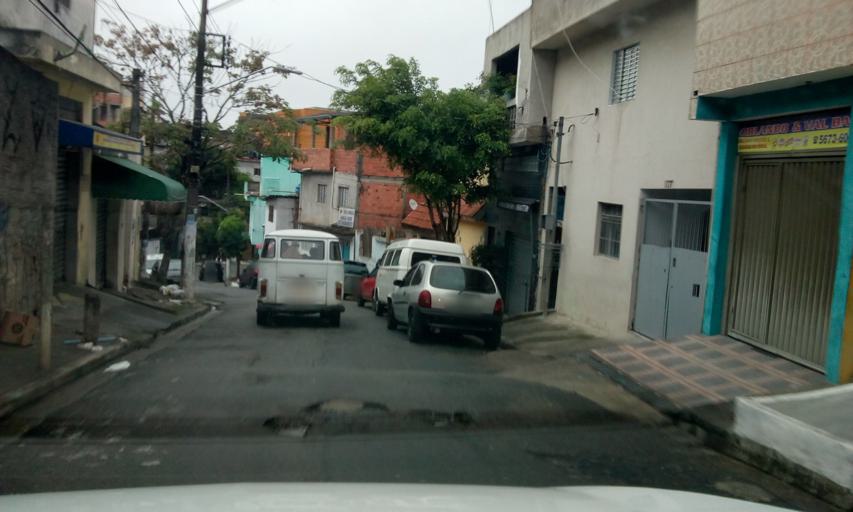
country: BR
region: Sao Paulo
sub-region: Diadema
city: Diadema
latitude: -23.6982
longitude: -46.6299
